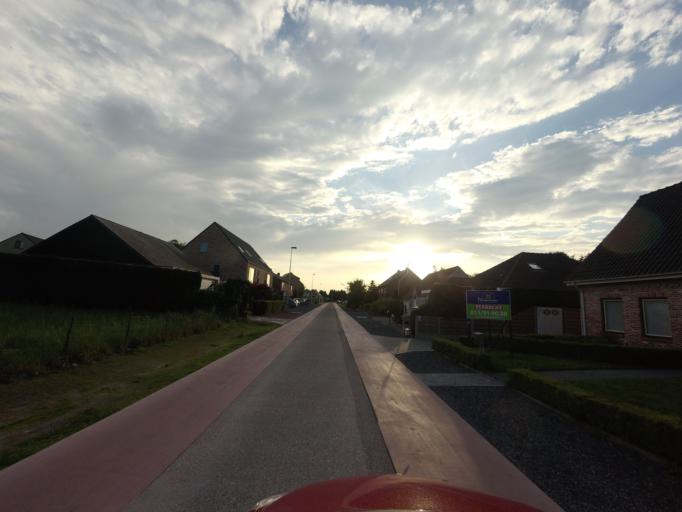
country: BE
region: Flanders
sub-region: Provincie Limburg
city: Lommel
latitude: 51.2328
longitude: 5.3302
